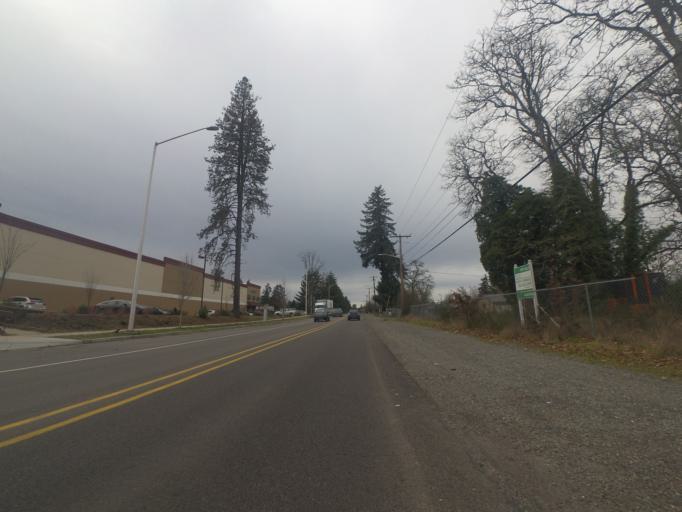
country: US
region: Washington
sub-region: Pierce County
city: McChord Air Force Base
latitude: 47.1213
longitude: -122.5295
